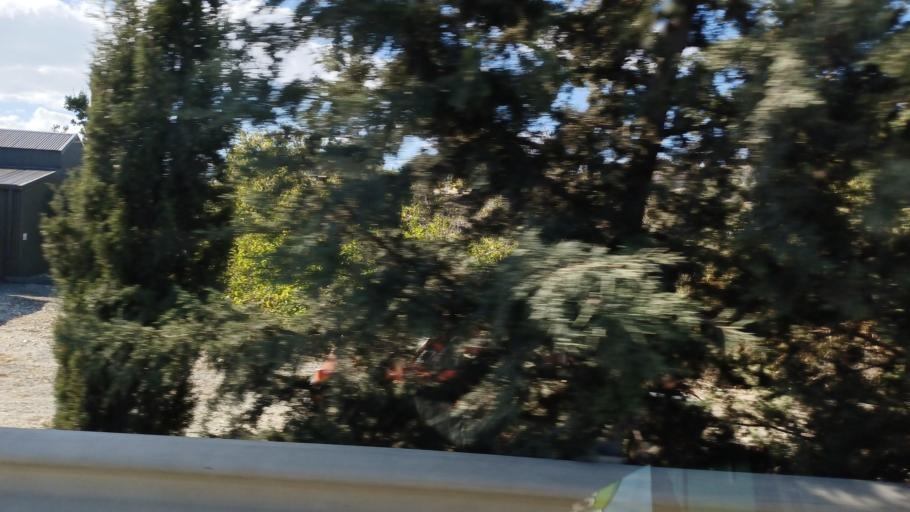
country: CY
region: Limassol
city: Pyrgos
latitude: 34.7421
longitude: 33.2110
